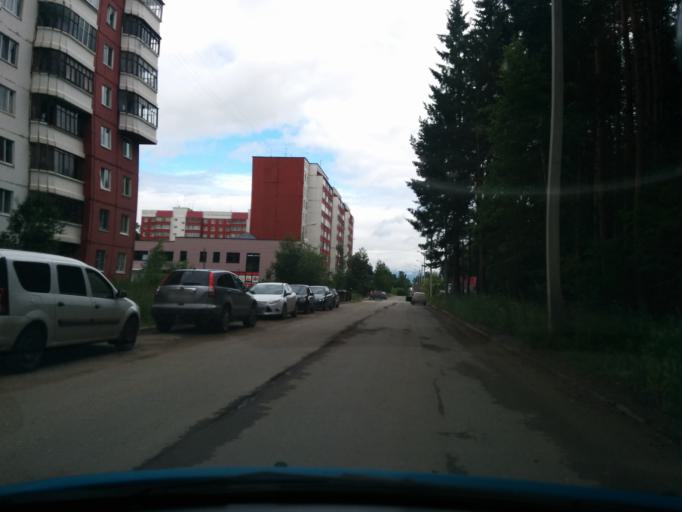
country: RU
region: Perm
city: Kondratovo
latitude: 58.0232
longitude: 56.0028
